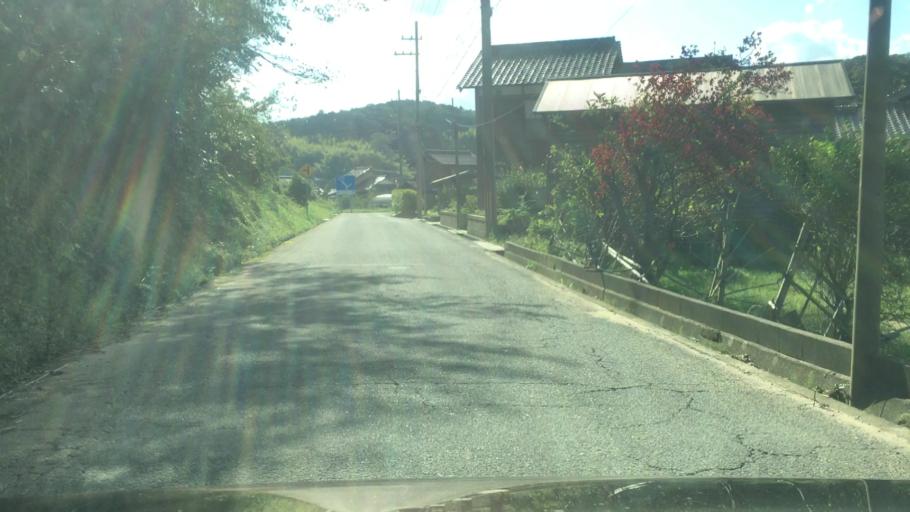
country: JP
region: Hyogo
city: Toyooka
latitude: 35.6506
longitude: 134.9676
